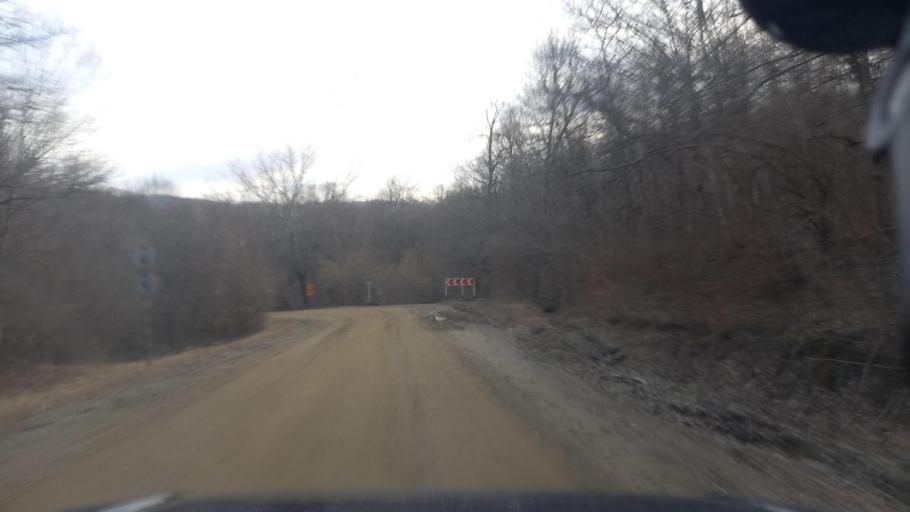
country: RU
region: Krasnodarskiy
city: Goryachiy Klyuch
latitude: 44.7073
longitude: 39.0136
